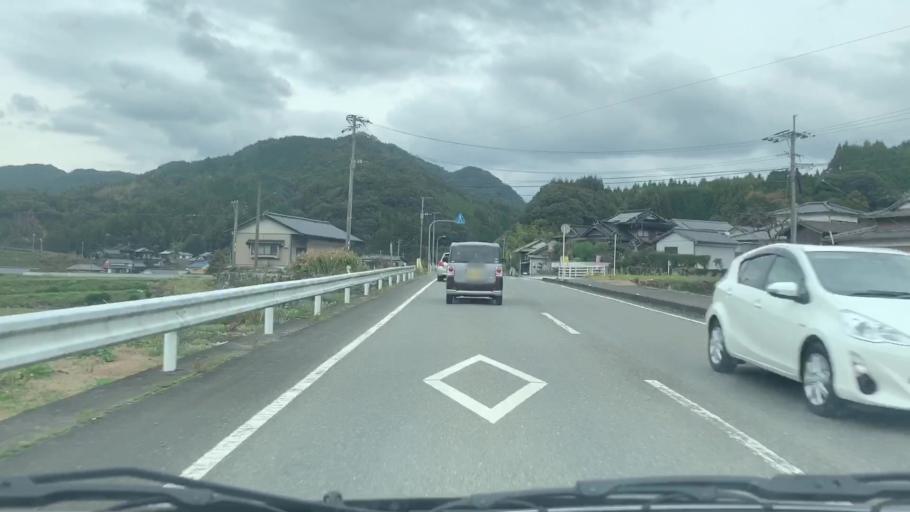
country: JP
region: Saga Prefecture
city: Ureshinomachi-shimojuku
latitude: 33.0909
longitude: 130.0264
